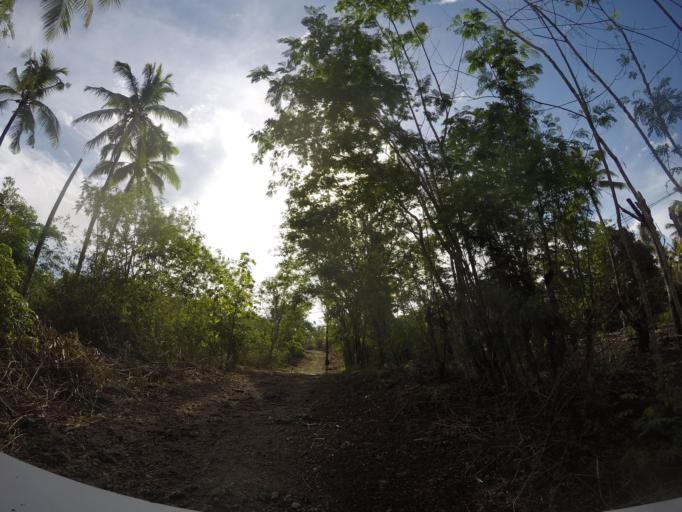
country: TL
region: Baucau
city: Baucau
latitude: -8.5019
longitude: 126.4531
